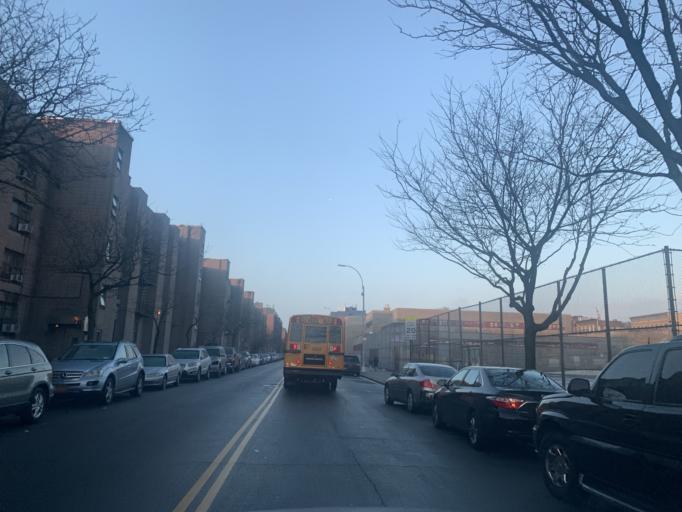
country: US
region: New York
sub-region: Kings County
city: Brooklyn
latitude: 40.6882
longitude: -73.9337
